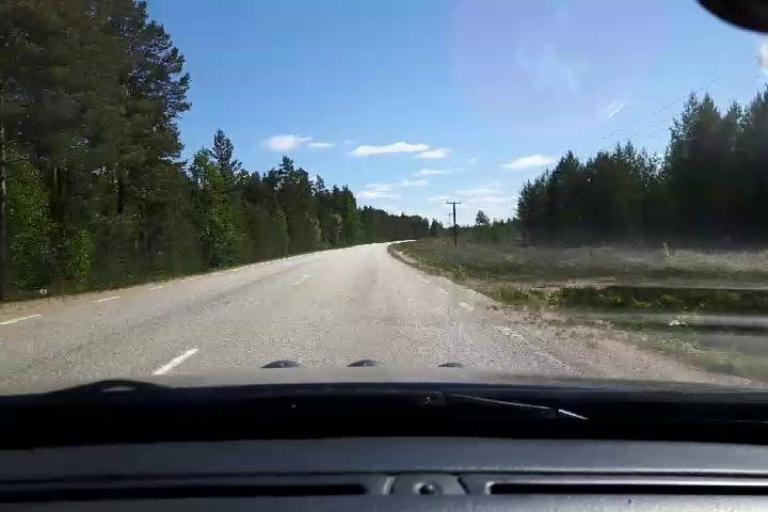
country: SE
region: Jaemtland
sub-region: Harjedalens Kommun
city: Sveg
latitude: 62.1125
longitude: 15.0556
